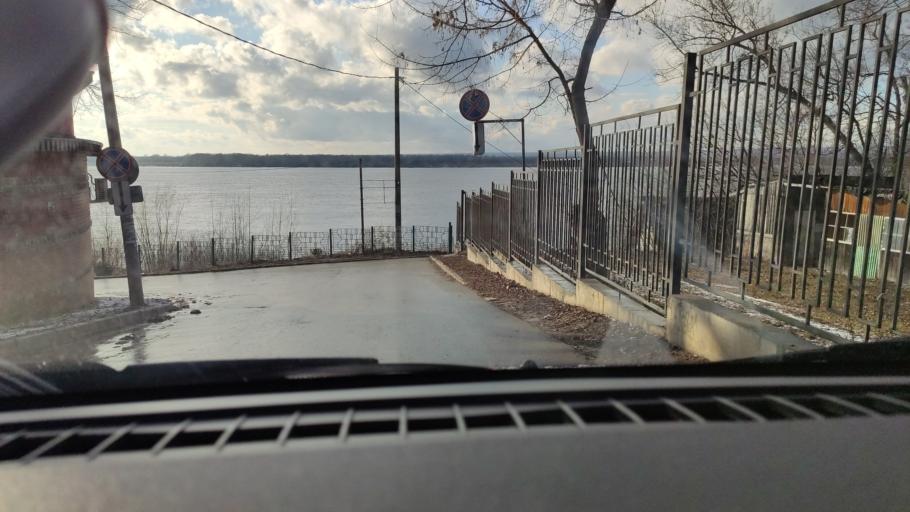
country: RU
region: Samara
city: Samara
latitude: 53.2634
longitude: 50.1832
